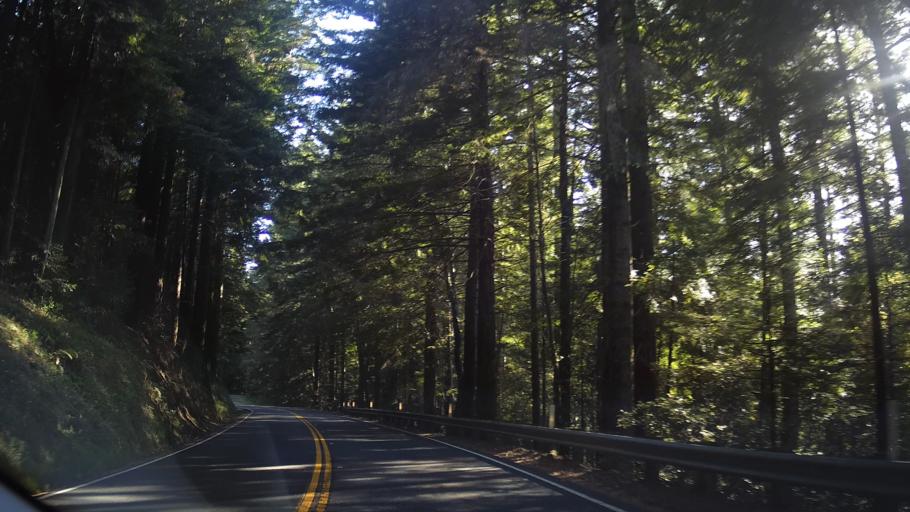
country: US
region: California
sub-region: Mendocino County
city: Fort Bragg
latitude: 39.3589
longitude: -123.6241
